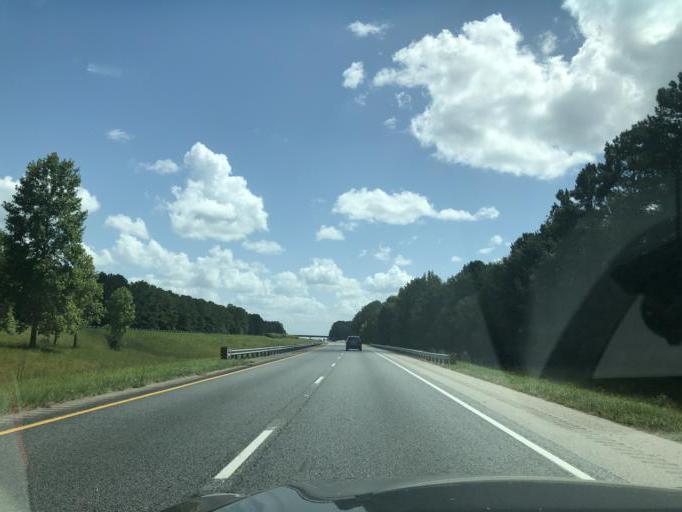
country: US
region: Georgia
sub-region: Troup County
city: La Grange
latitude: 32.9708
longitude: -84.9553
